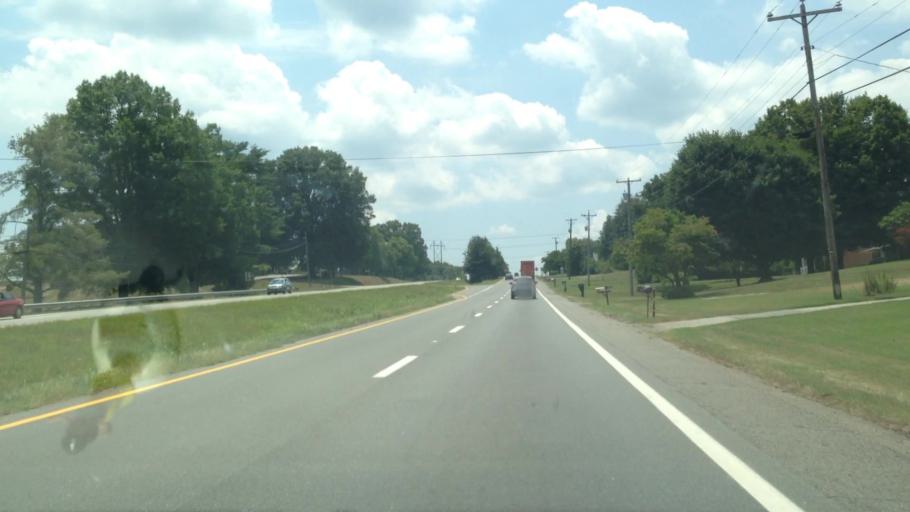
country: US
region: Virginia
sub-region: Henry County
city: Chatmoss
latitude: 36.6091
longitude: -79.8615
